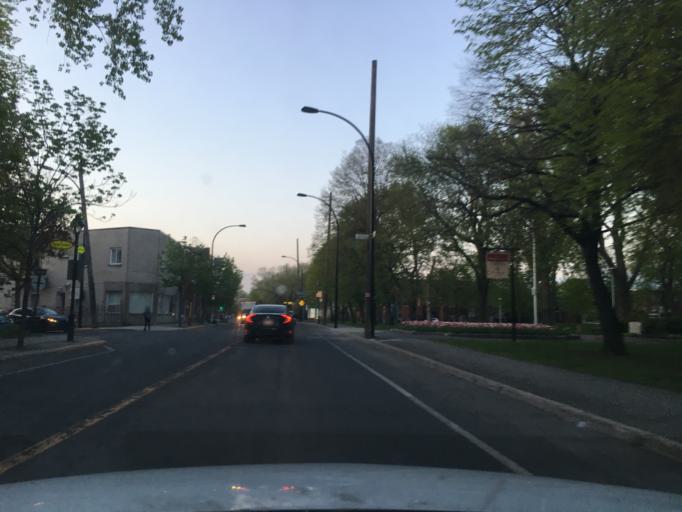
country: CA
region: Quebec
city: Westmount
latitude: 45.4753
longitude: -73.5607
